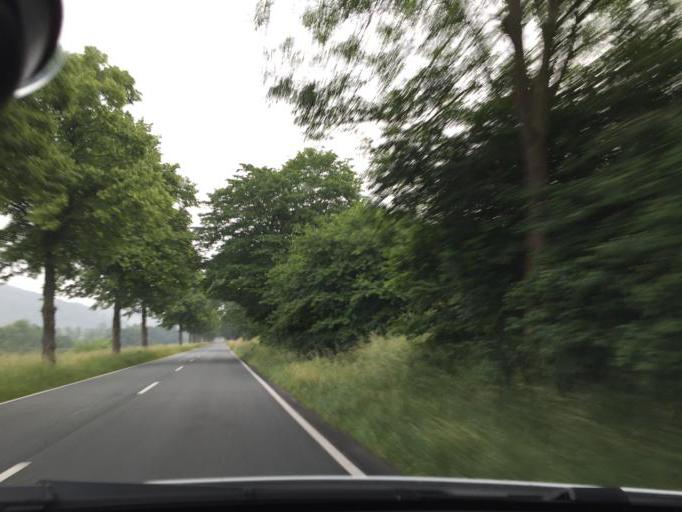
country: DE
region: Lower Saxony
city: Bad Pyrmont
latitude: 51.9802
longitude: 9.2982
